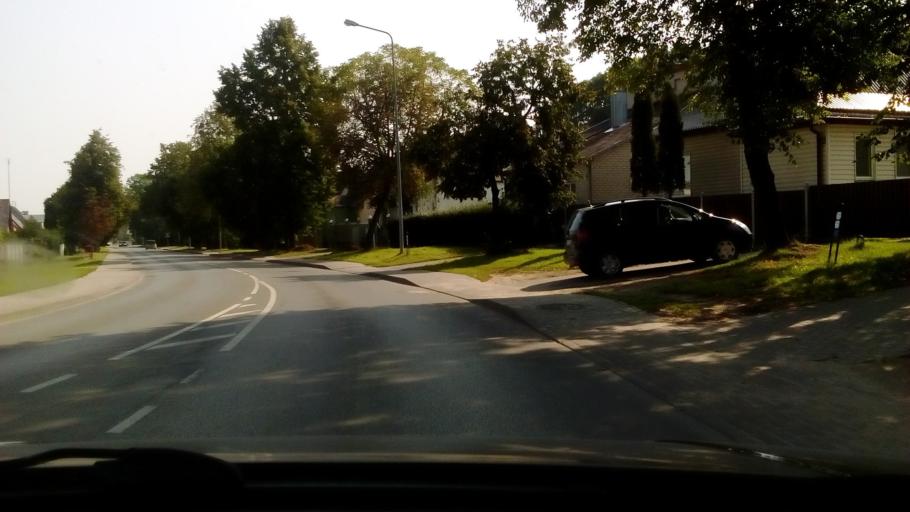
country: LT
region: Alytaus apskritis
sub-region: Alytus
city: Alytus
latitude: 54.4025
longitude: 24.0390
